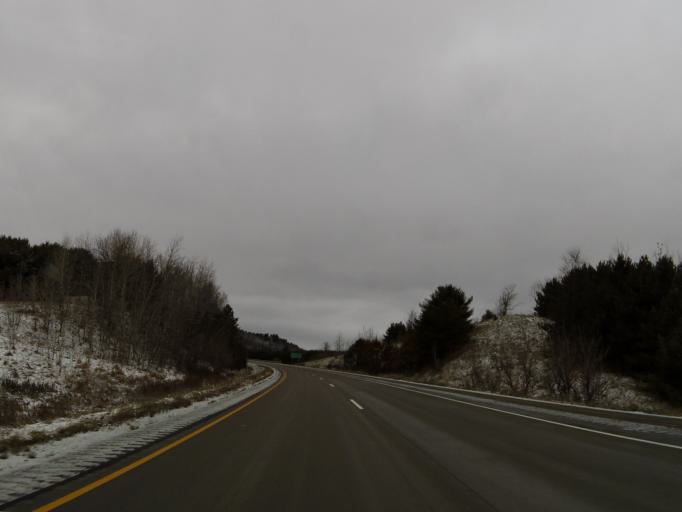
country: US
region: Wisconsin
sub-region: Trempealeau County
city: Osseo
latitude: 44.4722
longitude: -91.0994
